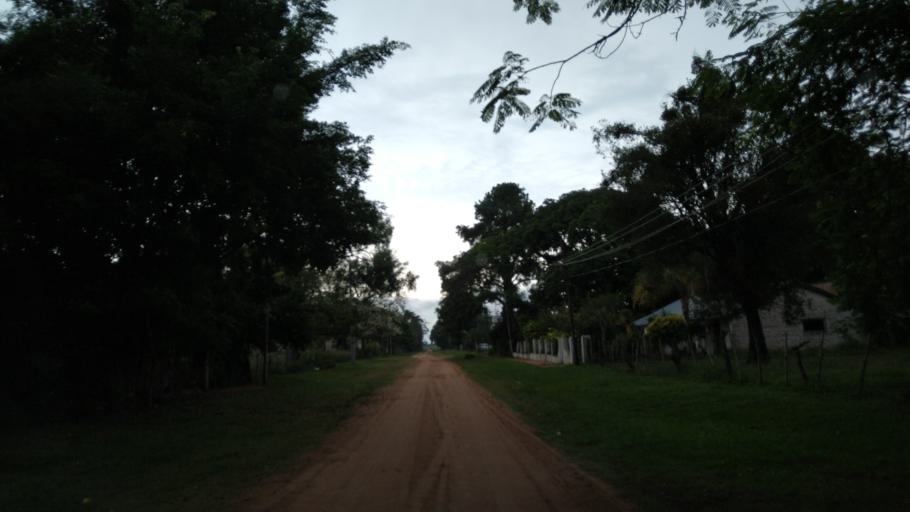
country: AR
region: Corrientes
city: Loreto
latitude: -27.7721
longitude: -57.2806
